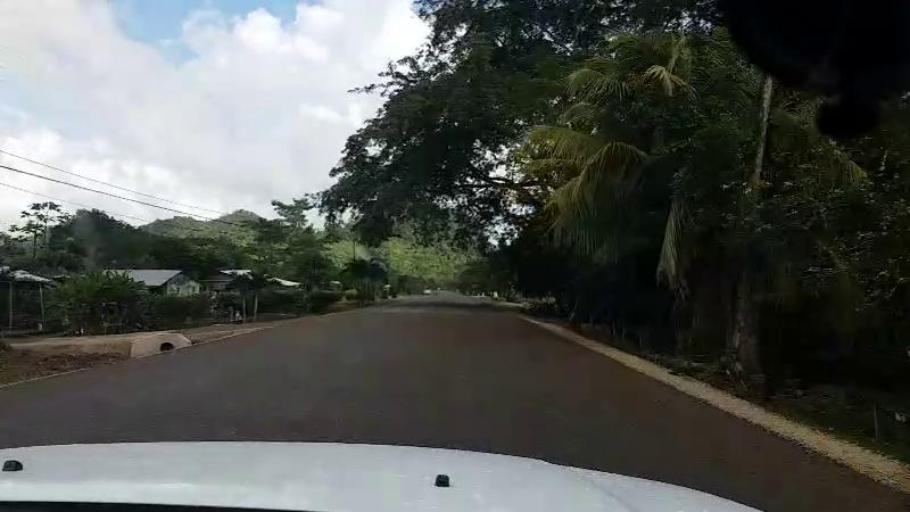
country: BZ
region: Cayo
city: Belmopan
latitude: 17.0915
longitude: -88.6318
